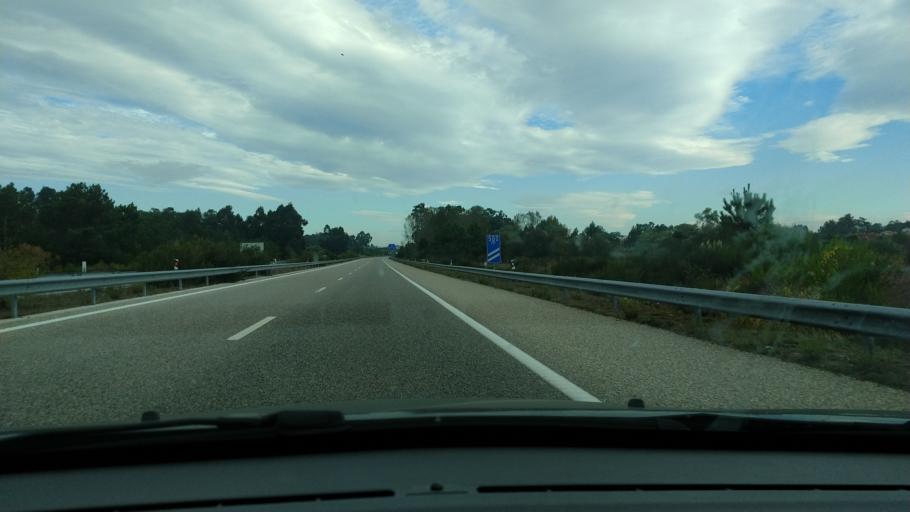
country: PT
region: Aveiro
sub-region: Vagos
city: Vagos
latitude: 40.4931
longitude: -8.6792
